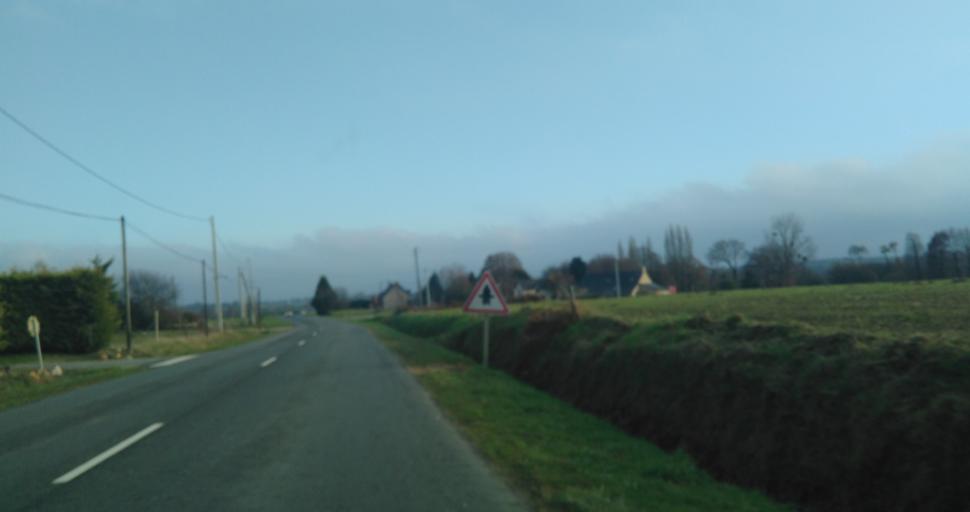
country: FR
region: Brittany
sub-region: Departement d'Ille-et-Vilaine
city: Saint-Meen-le-Grand
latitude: 48.1778
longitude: -2.1431
